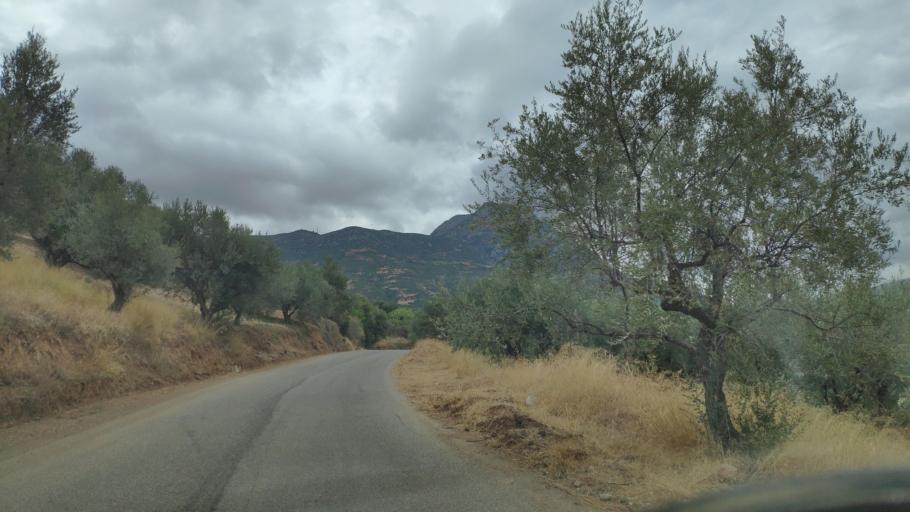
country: GR
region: West Greece
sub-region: Nomos Achaias
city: Temeni
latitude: 38.1740
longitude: 22.1424
